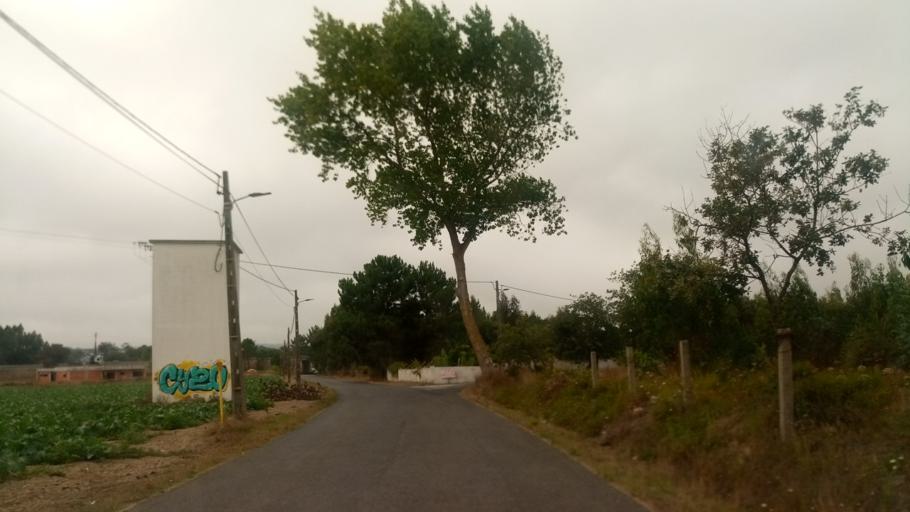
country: PT
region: Leiria
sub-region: Caldas da Rainha
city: Caldas da Rainha
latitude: 39.4197
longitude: -9.1465
